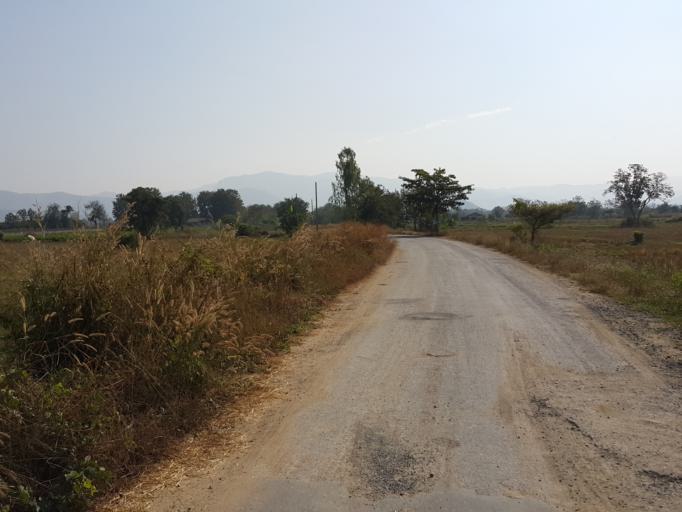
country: TH
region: Chiang Mai
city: San Kamphaeng
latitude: 18.6895
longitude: 99.1270
